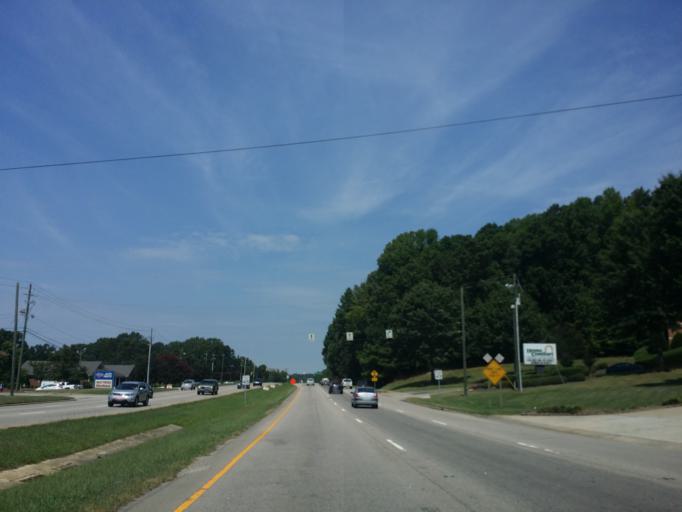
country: US
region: North Carolina
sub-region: Wake County
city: West Raleigh
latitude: 35.8644
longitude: -78.7144
